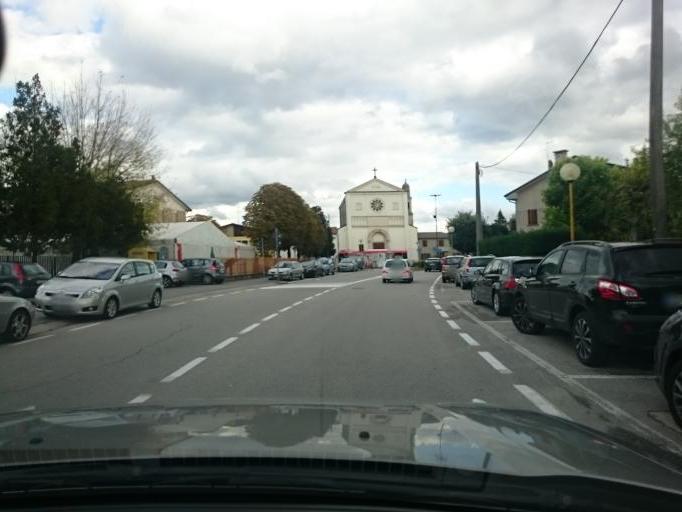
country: IT
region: Veneto
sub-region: Provincia di Padova
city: Ponte San Nicolo
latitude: 45.3624
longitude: 11.9072
